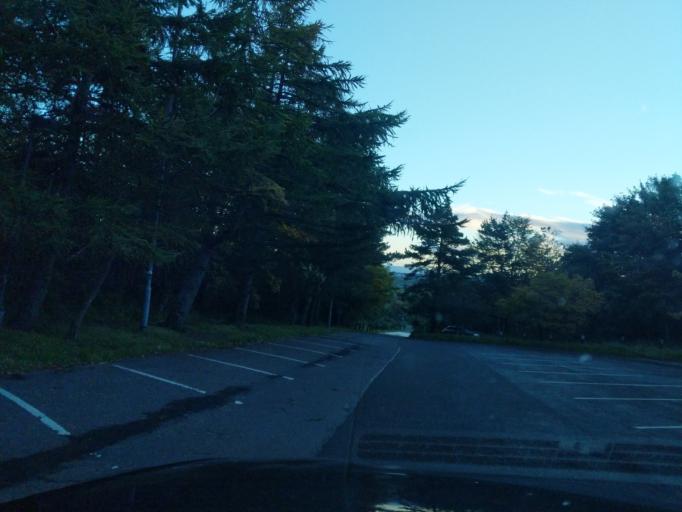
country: GB
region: Scotland
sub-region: Edinburgh
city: Colinton
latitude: 55.8878
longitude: -3.2109
